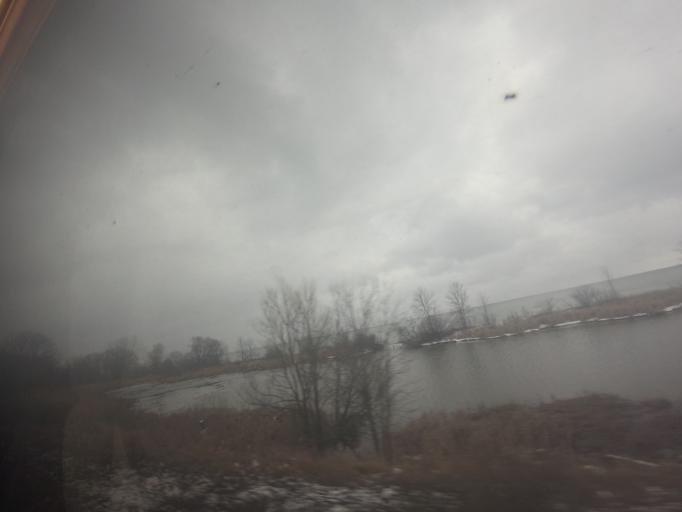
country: CA
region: Ontario
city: Cobourg
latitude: 43.9540
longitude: -78.2477
